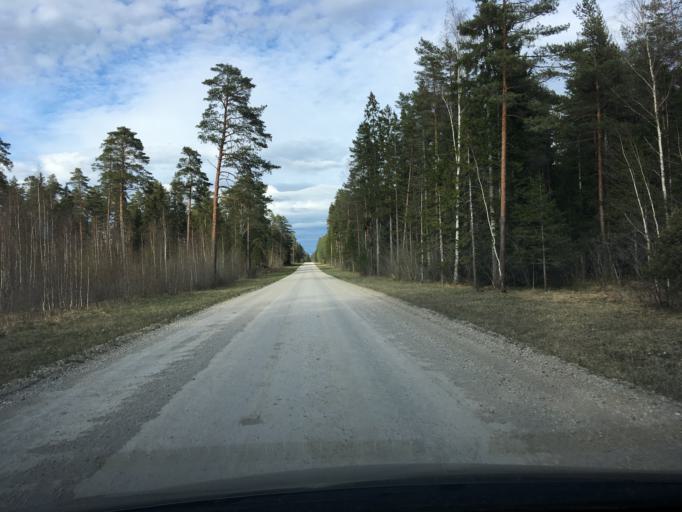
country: EE
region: Raplamaa
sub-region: Maerjamaa vald
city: Marjamaa
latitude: 59.0126
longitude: 24.4087
